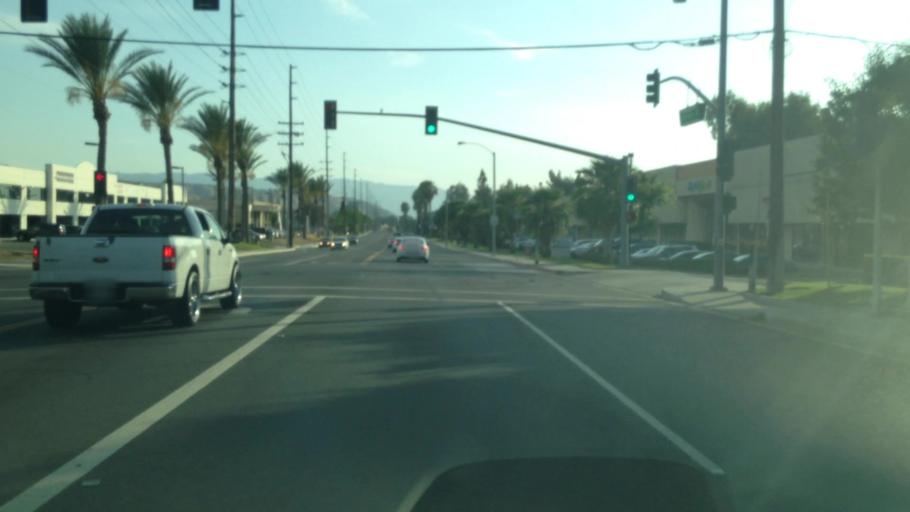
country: US
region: California
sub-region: Riverside County
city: Riverside
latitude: 33.9101
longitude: -117.4486
